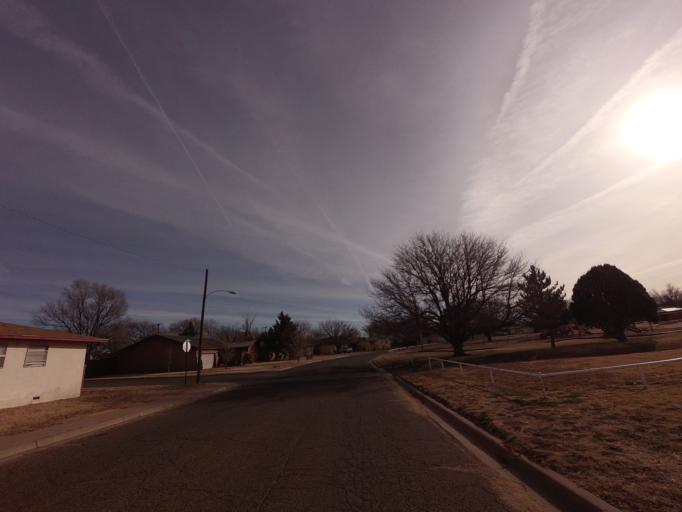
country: US
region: New Mexico
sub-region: Curry County
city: Clovis
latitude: 34.4135
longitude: -103.2184
